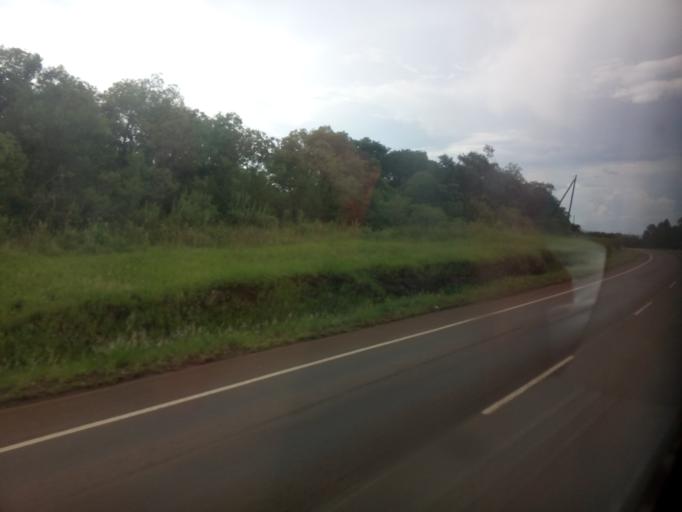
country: AR
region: Misiones
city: Santa Ana
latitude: -27.4035
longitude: -55.6024
